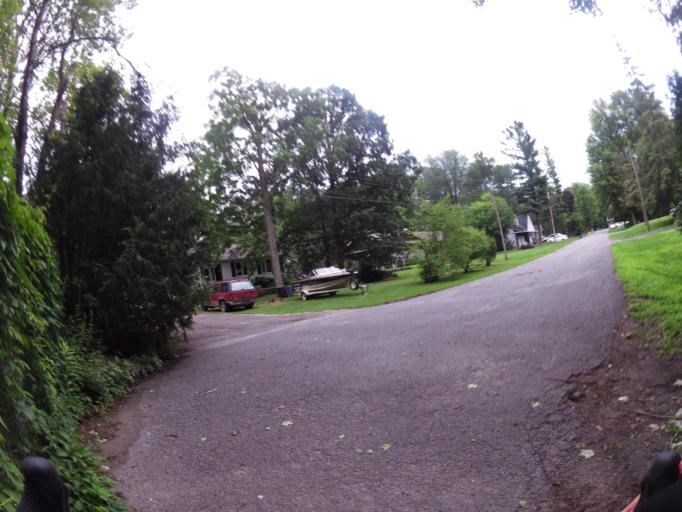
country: CA
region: Ontario
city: Ottawa
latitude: 45.3213
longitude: -75.7193
